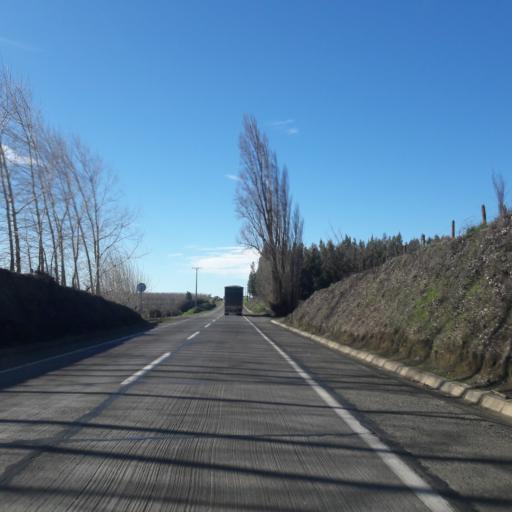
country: CL
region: Araucania
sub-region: Provincia de Malleco
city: Angol
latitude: -37.7425
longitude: -72.6080
